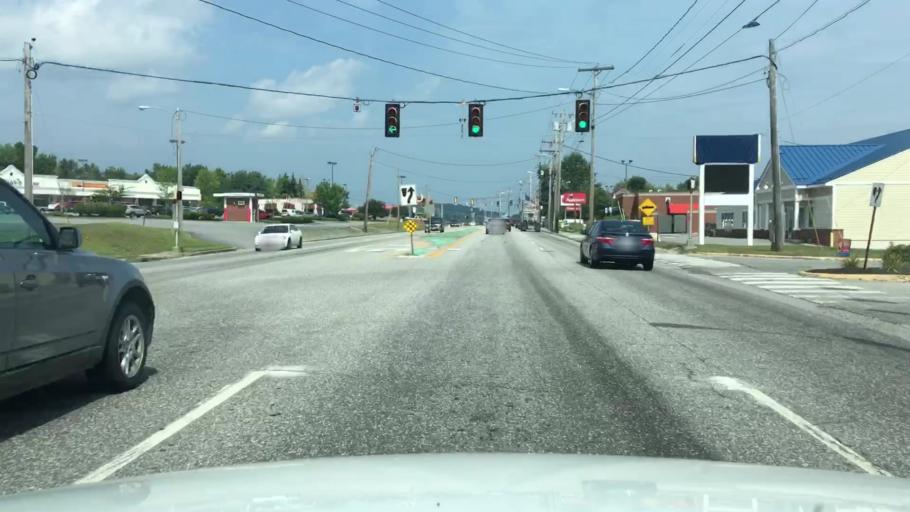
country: US
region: Maine
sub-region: Androscoggin County
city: Lewiston
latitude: 44.1227
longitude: -70.2250
